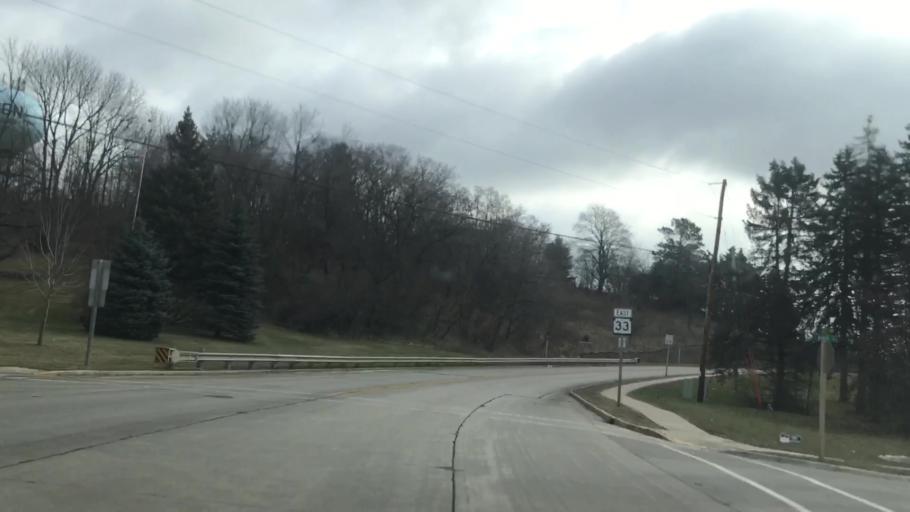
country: US
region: Wisconsin
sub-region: Dodge County
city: Horicon
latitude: 43.4516
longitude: -88.6232
